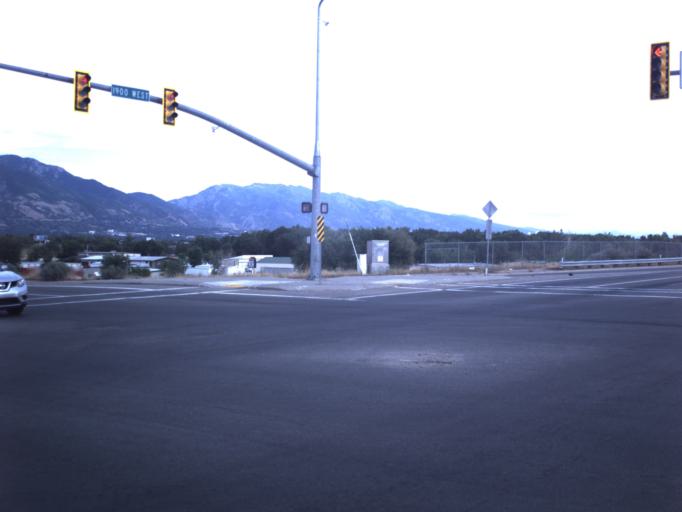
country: US
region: Utah
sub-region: Weber County
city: Marriott-Slaterville
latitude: 41.2450
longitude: -112.0254
